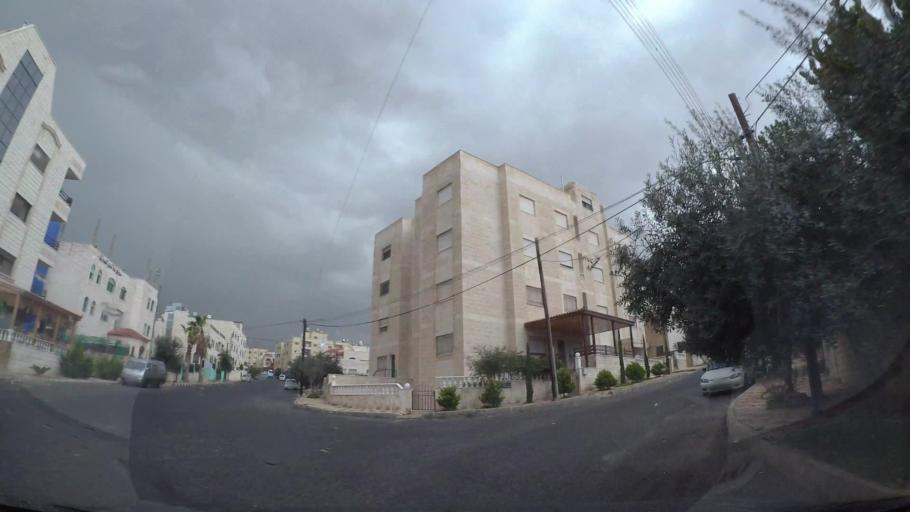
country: JO
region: Amman
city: Amman
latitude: 32.0073
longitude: 35.9594
